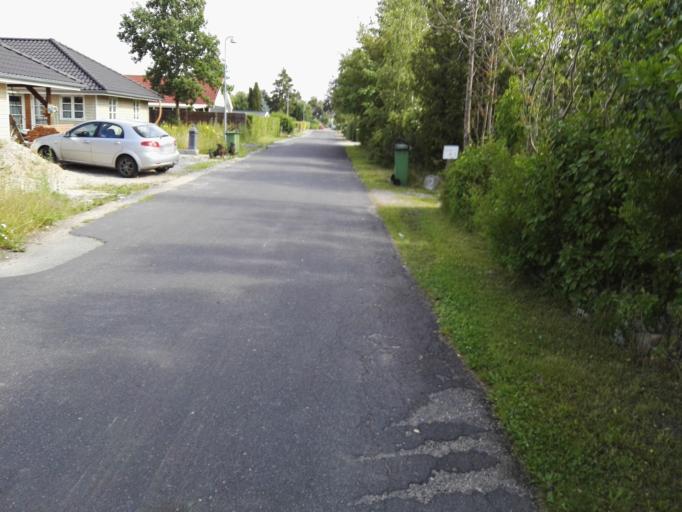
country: DK
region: Zealand
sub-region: Roskilde Kommune
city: Jyllinge
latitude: 55.7707
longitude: 12.1051
